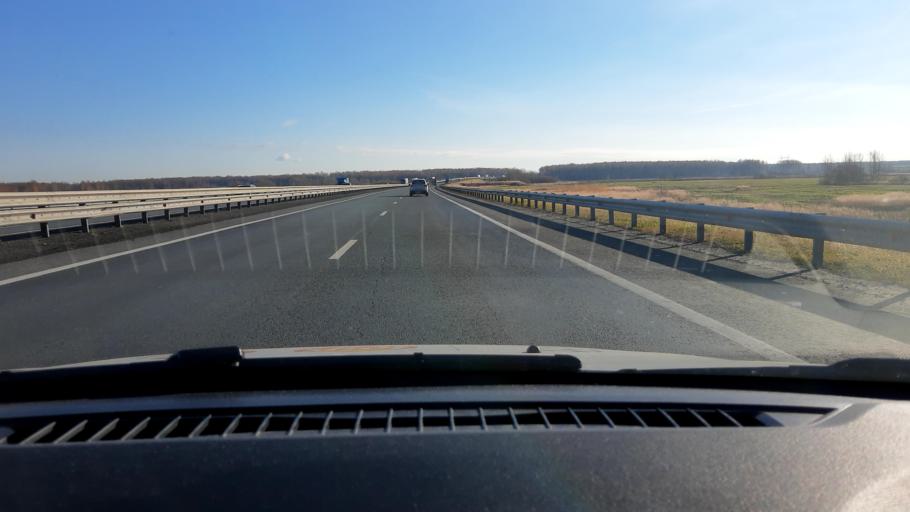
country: RU
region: Nizjnij Novgorod
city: Burevestnik
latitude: 56.1246
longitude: 43.7942
